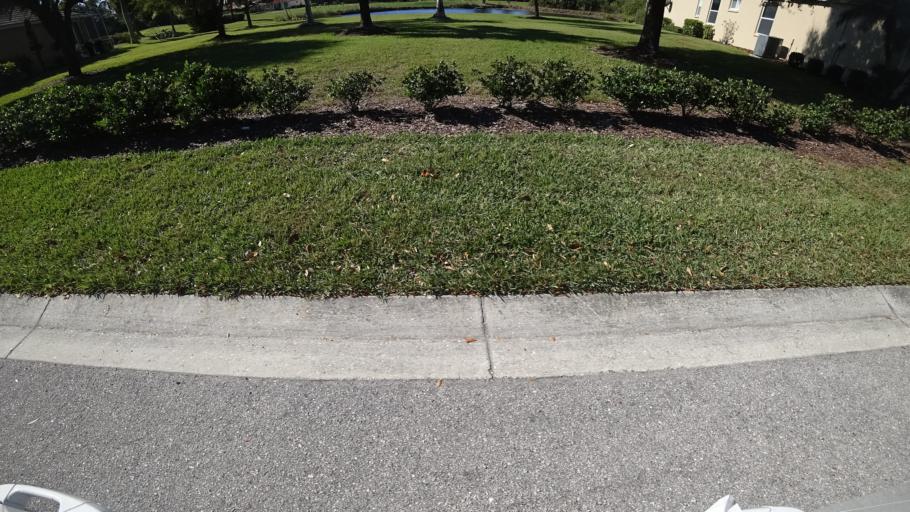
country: US
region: Florida
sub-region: Sarasota County
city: Desoto Lakes
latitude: 27.4218
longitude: -82.4614
